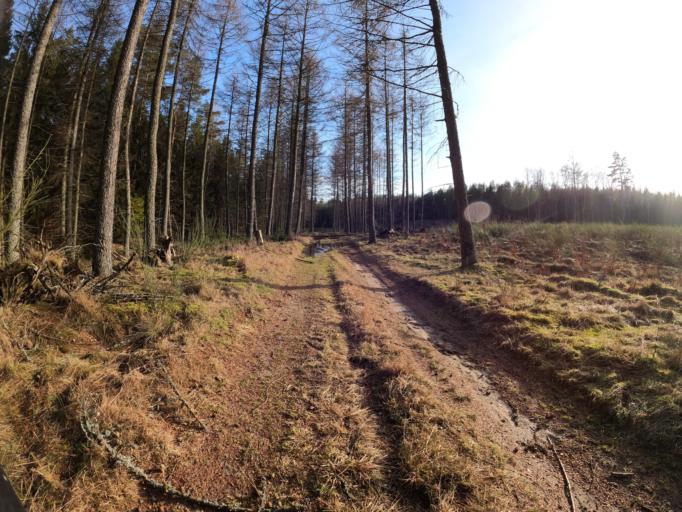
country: PL
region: West Pomeranian Voivodeship
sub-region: Powiat koszalinski
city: Polanow
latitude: 54.1892
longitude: 16.6722
